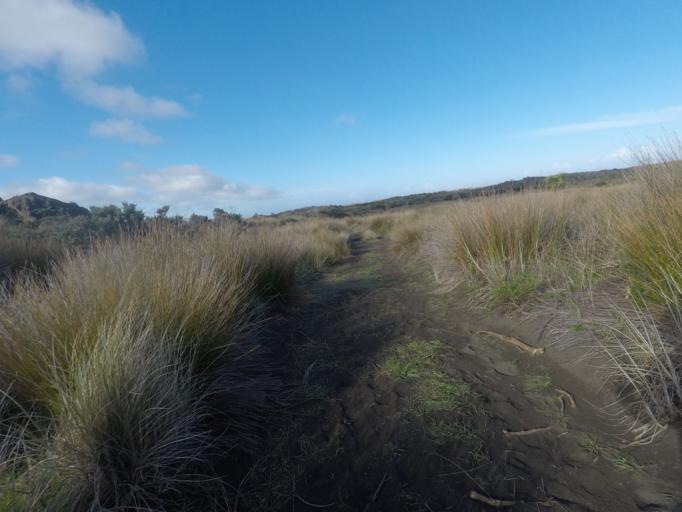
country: NZ
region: Auckland
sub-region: Auckland
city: Titirangi
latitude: -37.0084
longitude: 174.4808
